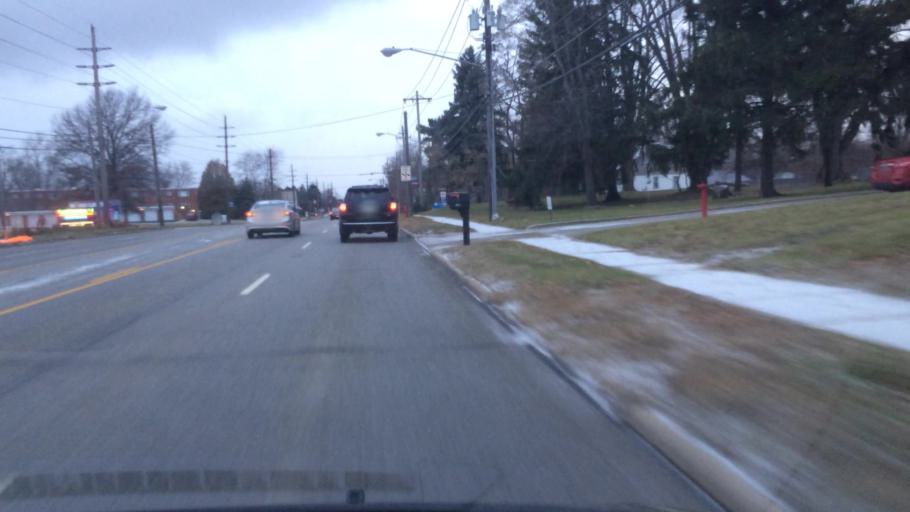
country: US
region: Ohio
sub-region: Cuyahoga County
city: Berea
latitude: 41.3722
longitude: -81.8356
